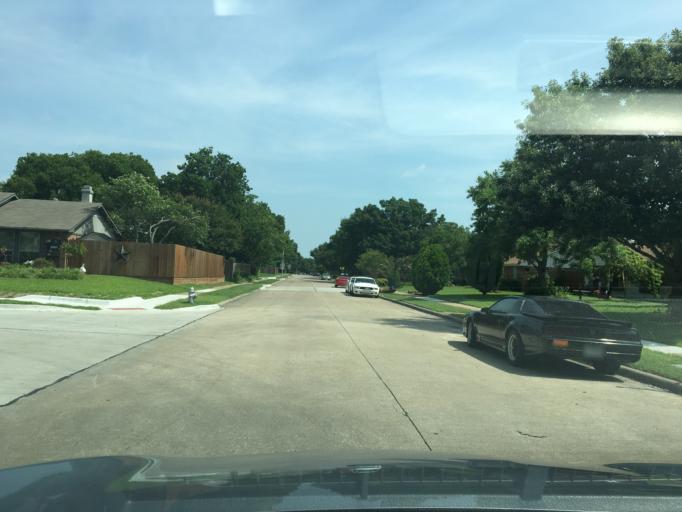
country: US
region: Texas
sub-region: Dallas County
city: Garland
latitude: 32.9265
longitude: -96.6715
